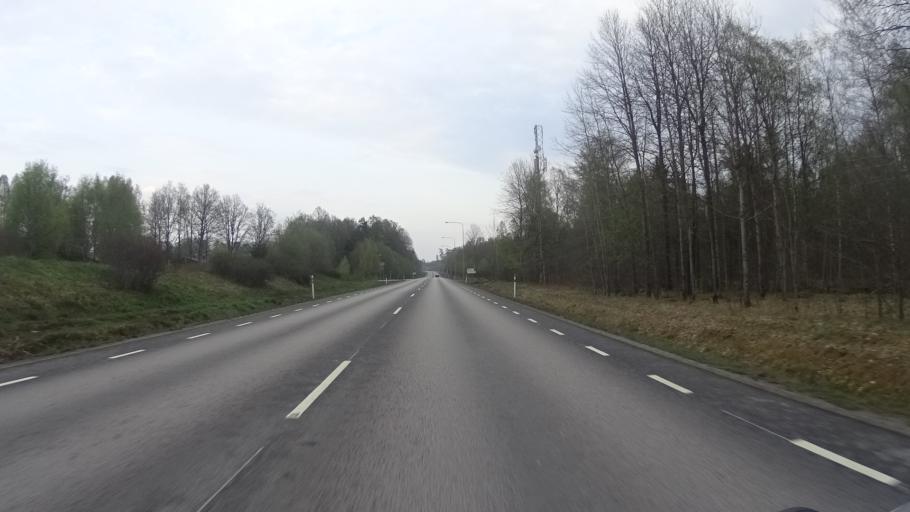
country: SE
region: Kronoberg
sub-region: Ljungby Kommun
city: Ljungby
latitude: 56.8215
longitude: 13.9532
